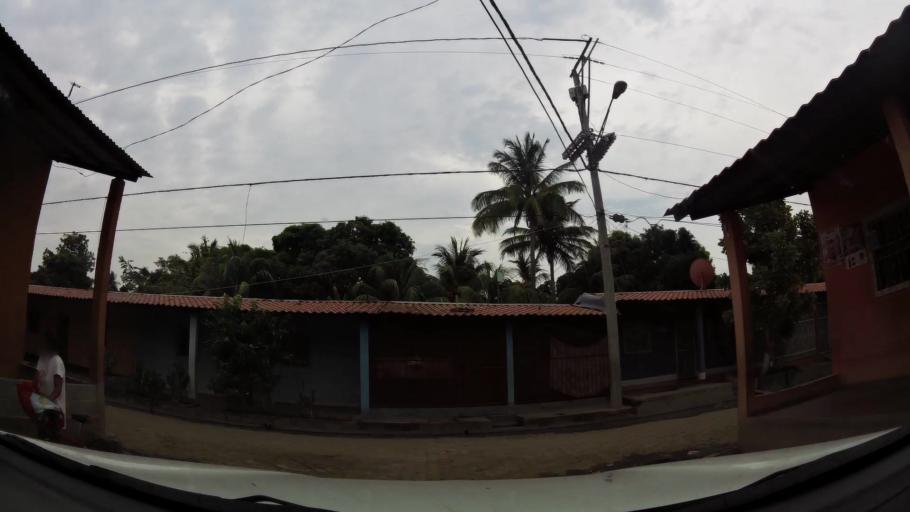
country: NI
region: Granada
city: Granada
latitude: 11.9344
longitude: -85.9448
